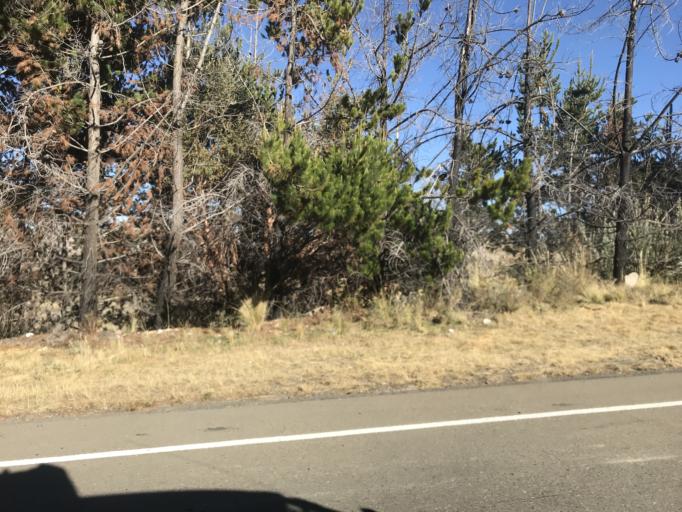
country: PE
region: Puno
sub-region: Yunguyo
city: Yunguyo
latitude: -16.1728
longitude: -68.9827
